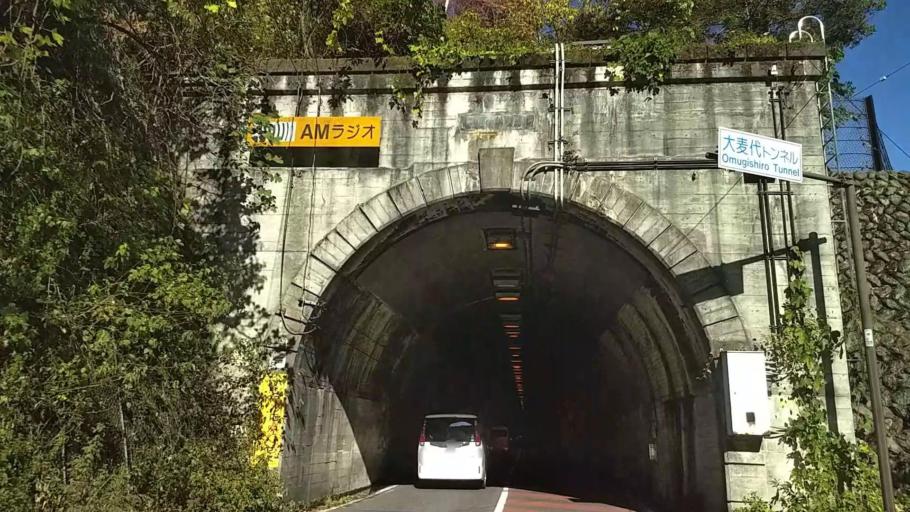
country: JP
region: Tokyo
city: Itsukaichi
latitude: 35.7902
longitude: 139.0426
